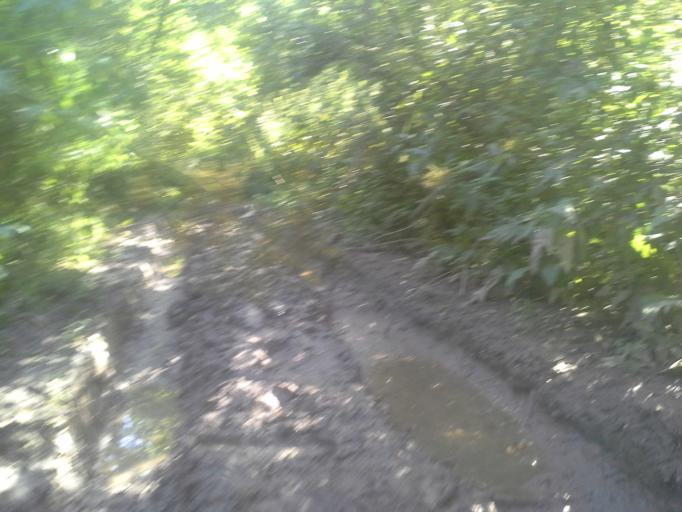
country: RU
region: Moskovskaya
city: Aprelevka
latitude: 55.4571
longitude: 37.0763
